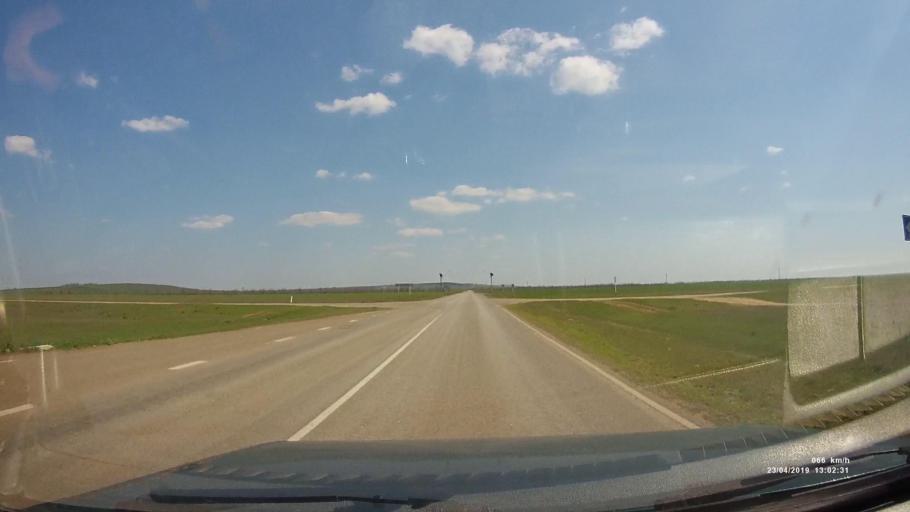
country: RU
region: Kalmykiya
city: Yashalta
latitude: 46.6002
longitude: 42.6703
